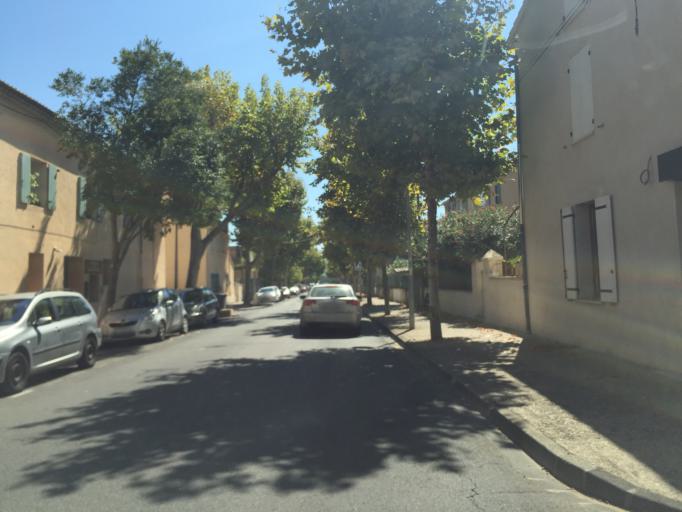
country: FR
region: Provence-Alpes-Cote d'Azur
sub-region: Departement du Vaucluse
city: Carpentras
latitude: 44.0485
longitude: 5.0480
